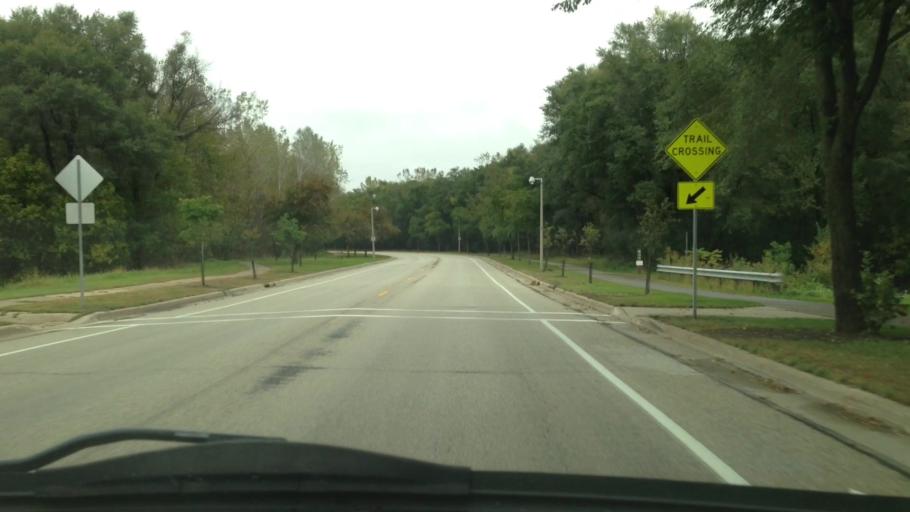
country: US
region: Minnesota
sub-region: Olmsted County
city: Rochester
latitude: 44.0564
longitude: -92.4676
